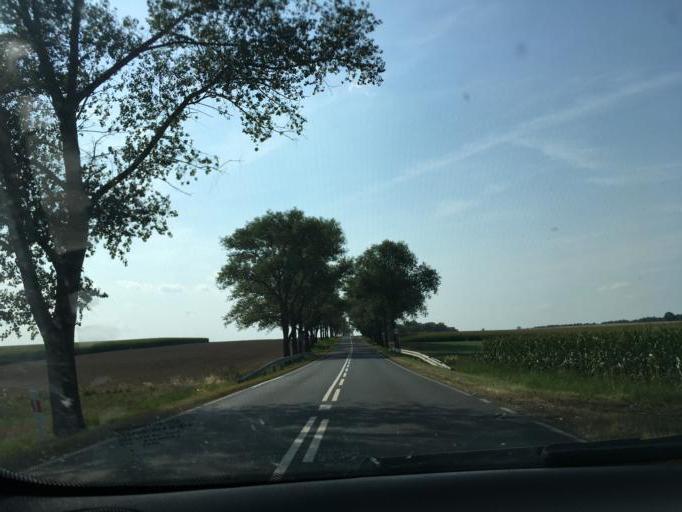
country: PL
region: Opole Voivodeship
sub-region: Powiat prudnicki
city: Laka Prudnicka
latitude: 50.4194
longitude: 17.4779
